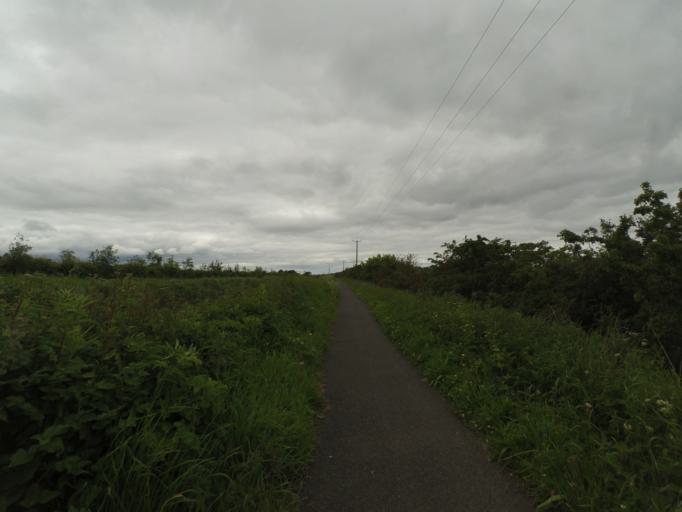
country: GB
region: Scotland
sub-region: West Lothian
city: Linlithgow
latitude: 55.9769
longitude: -3.5482
